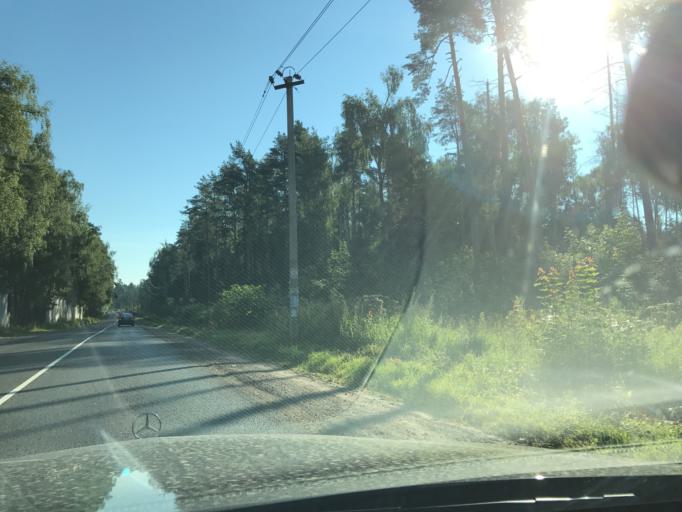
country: RU
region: Moskovskaya
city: Sverdlovskiy
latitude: 55.8621
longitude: 38.1444
